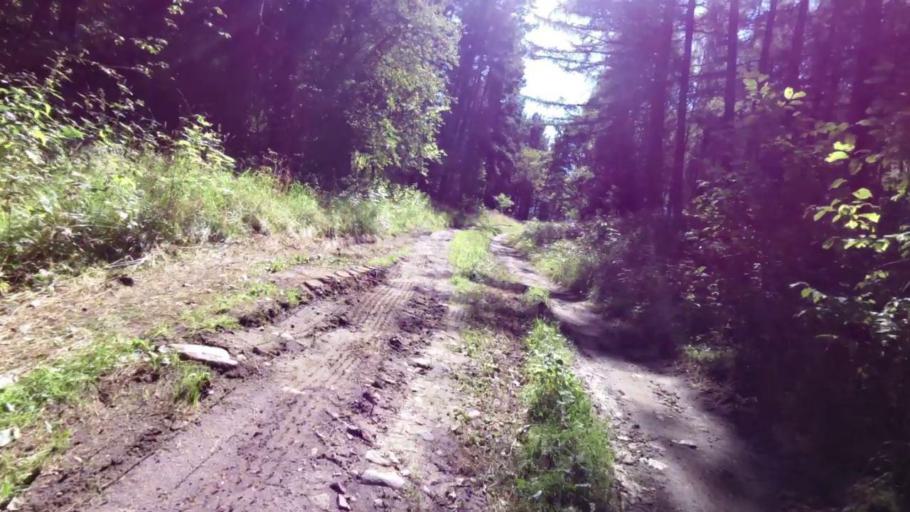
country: PL
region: West Pomeranian Voivodeship
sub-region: Powiat szczecinecki
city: Bialy Bor
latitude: 53.8561
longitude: 16.7697
